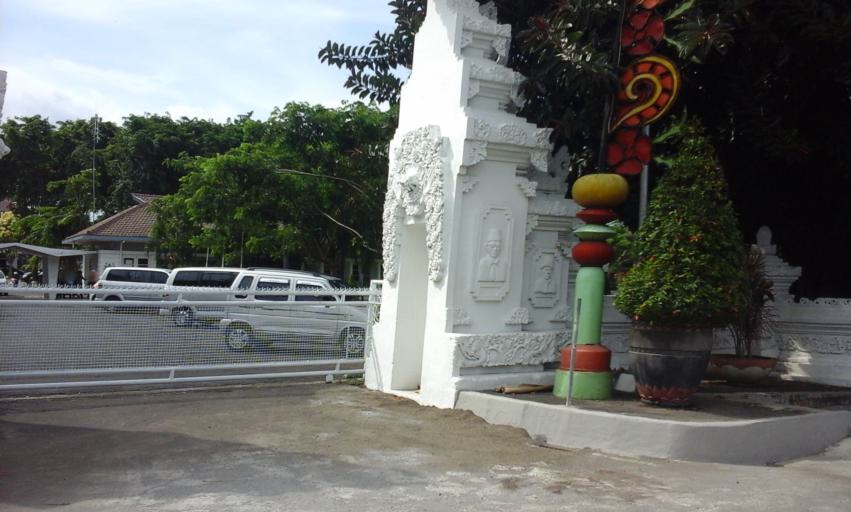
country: ID
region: East Java
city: Krajan Selatan
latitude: -8.2235
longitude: 114.3673
